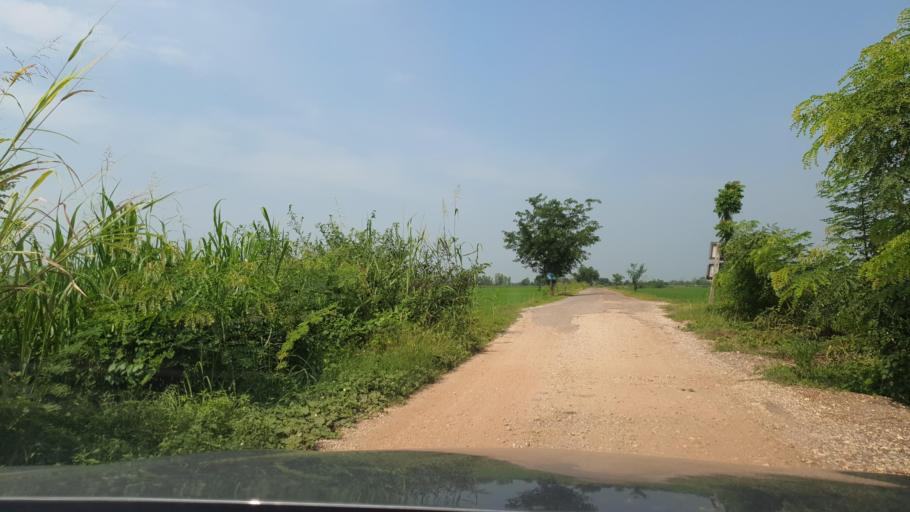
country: TH
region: Phitsanulok
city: Bang Rakam
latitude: 16.8037
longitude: 100.1135
